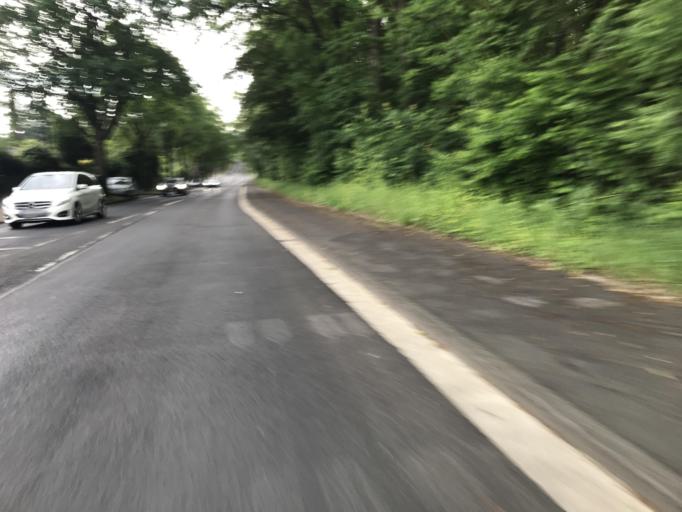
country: DE
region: Hesse
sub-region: Regierungsbezirk Kassel
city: Baunatal
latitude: 51.2993
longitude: 9.4336
